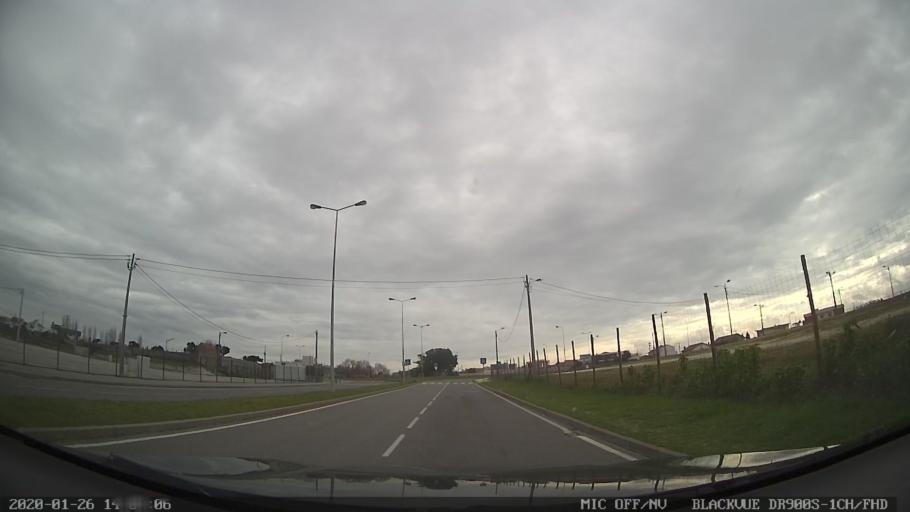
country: PT
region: Aveiro
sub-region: Aveiro
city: Aradas
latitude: 40.6324
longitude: -8.6307
